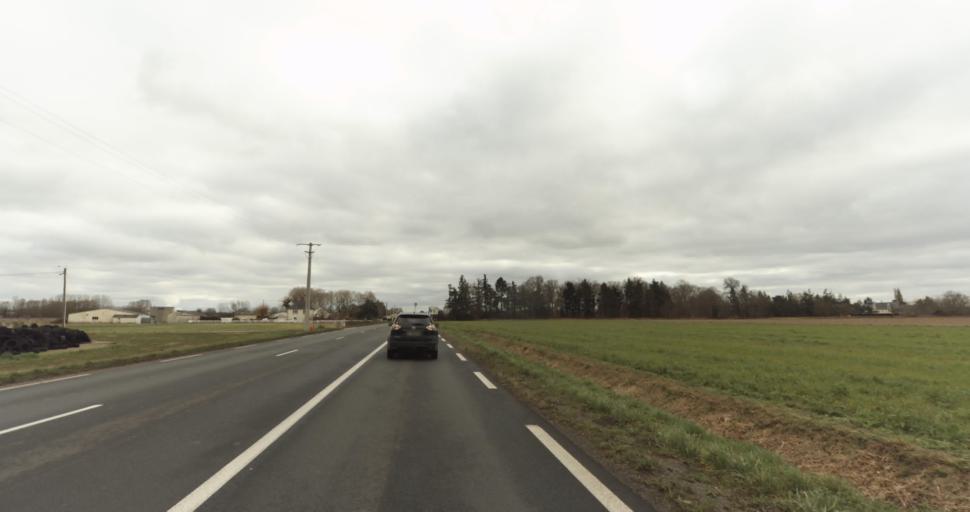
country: FR
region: Pays de la Loire
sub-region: Departement de Maine-et-Loire
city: Vivy
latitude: 47.3091
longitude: -0.0400
